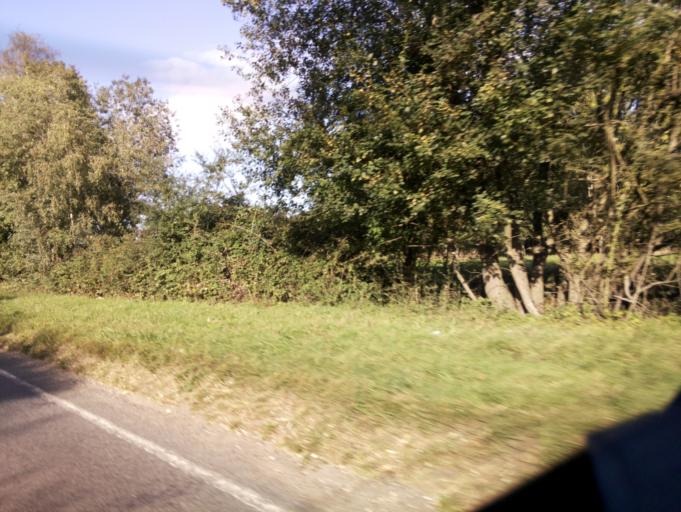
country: GB
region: England
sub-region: Hampshire
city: Tadley
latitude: 51.3190
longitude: -1.1212
